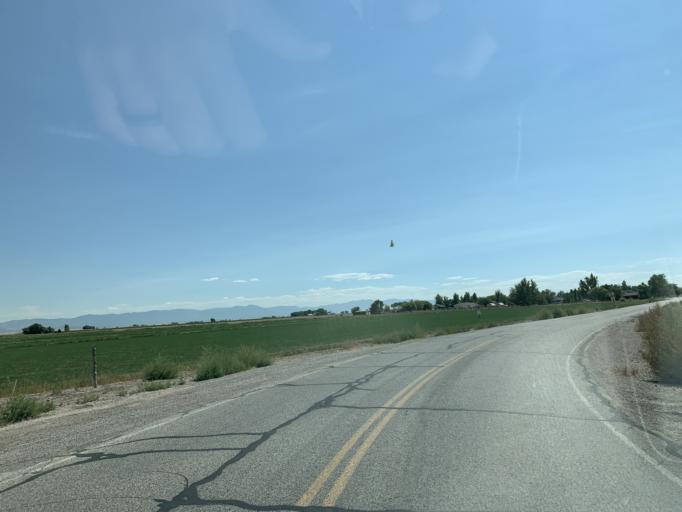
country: US
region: Utah
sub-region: Millard County
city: Delta
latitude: 39.3405
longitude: -112.6148
